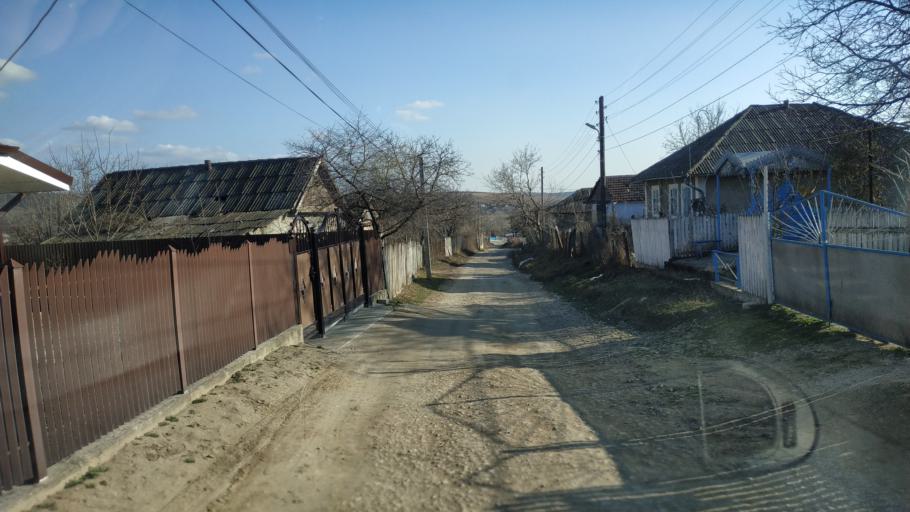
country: MD
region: Hincesti
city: Hincesti
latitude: 46.7326
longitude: 28.5124
